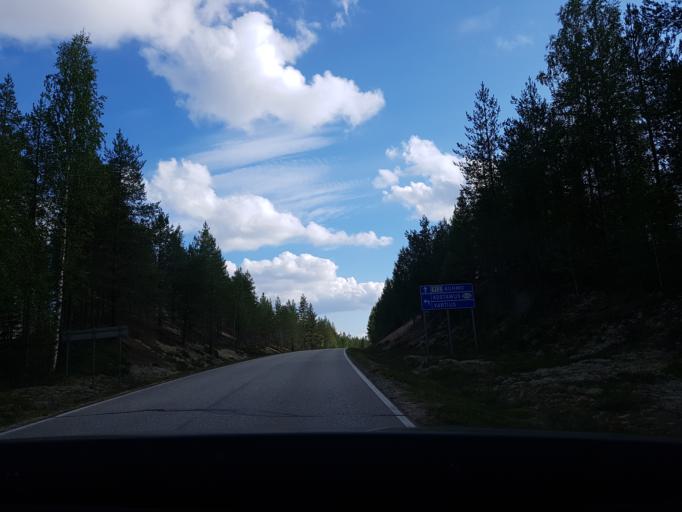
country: FI
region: Kainuu
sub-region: Kehys-Kainuu
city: Kuhmo
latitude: 64.6248
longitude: 29.6975
